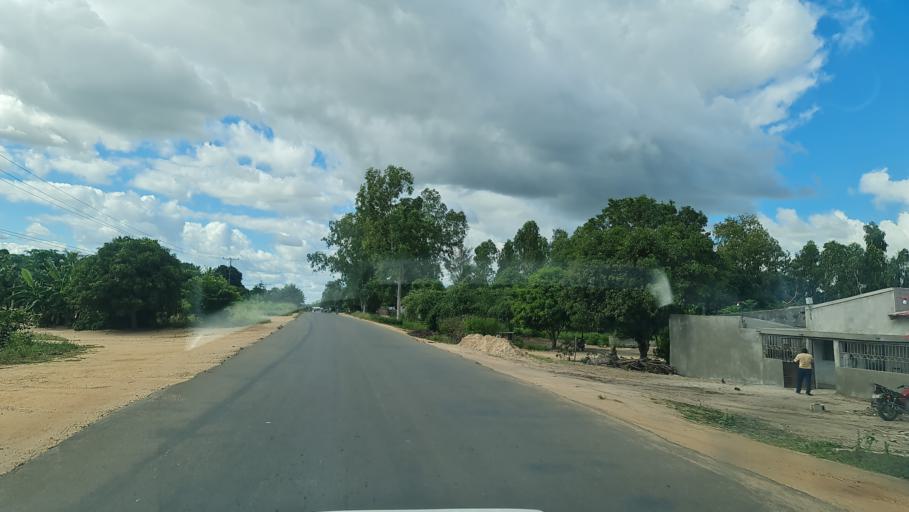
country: MZ
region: Zambezia
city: Quelimane
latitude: -17.6006
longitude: 36.8052
